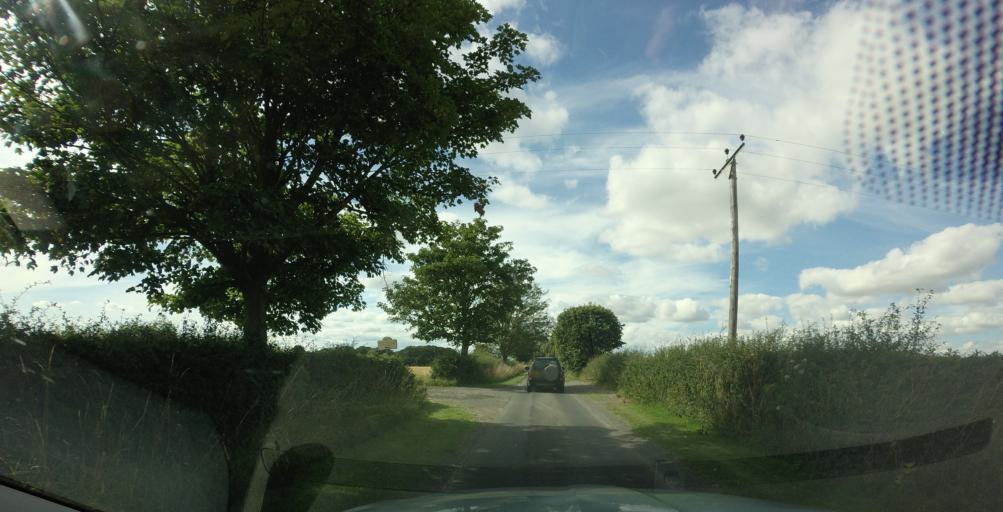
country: GB
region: England
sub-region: North Yorkshire
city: Ripon
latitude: 54.1136
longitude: -1.4805
